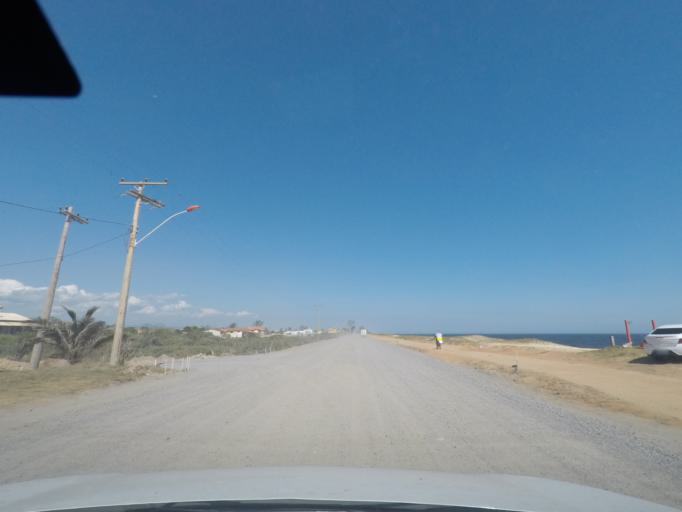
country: BR
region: Rio de Janeiro
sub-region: Marica
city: Marica
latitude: -22.9709
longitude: -42.9481
